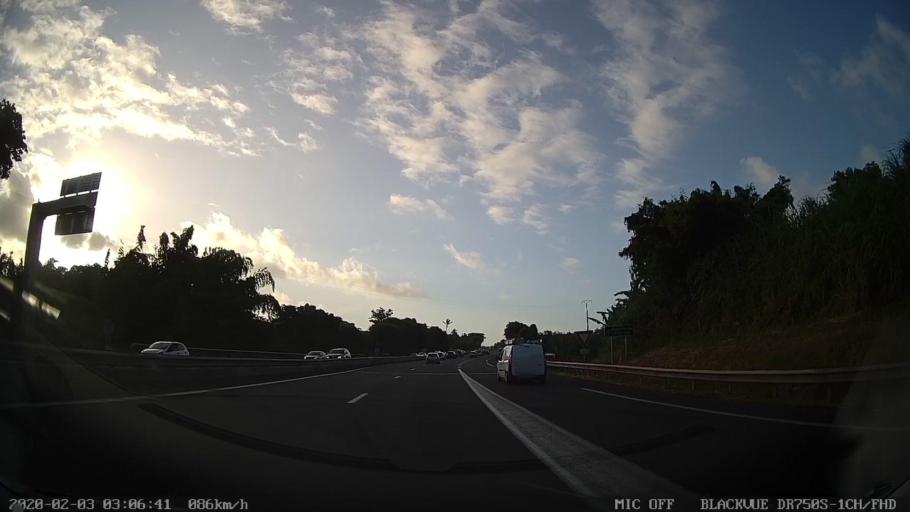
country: RE
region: Reunion
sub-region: Reunion
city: Saint-Andre
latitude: -20.9424
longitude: 55.6457
